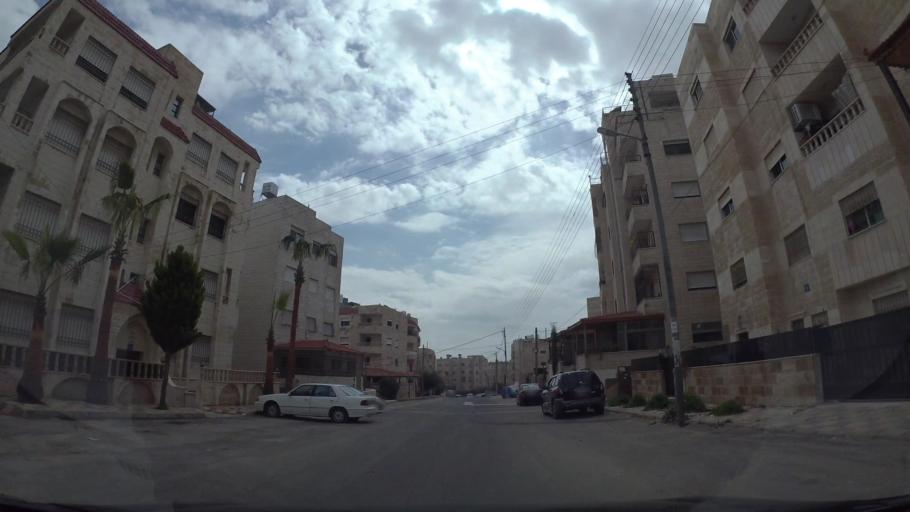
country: JO
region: Amman
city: Amman
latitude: 31.9900
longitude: 35.9242
